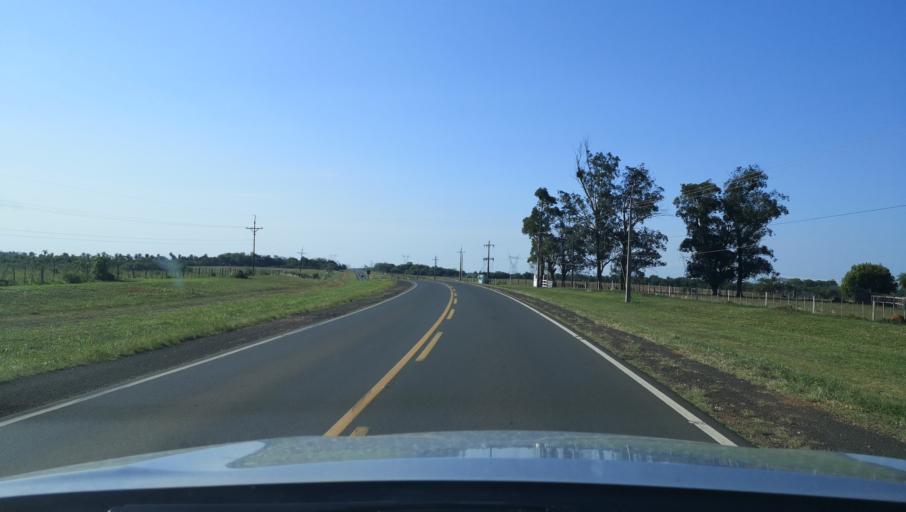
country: PY
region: Misiones
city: Santa Maria
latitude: -26.8064
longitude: -57.0201
